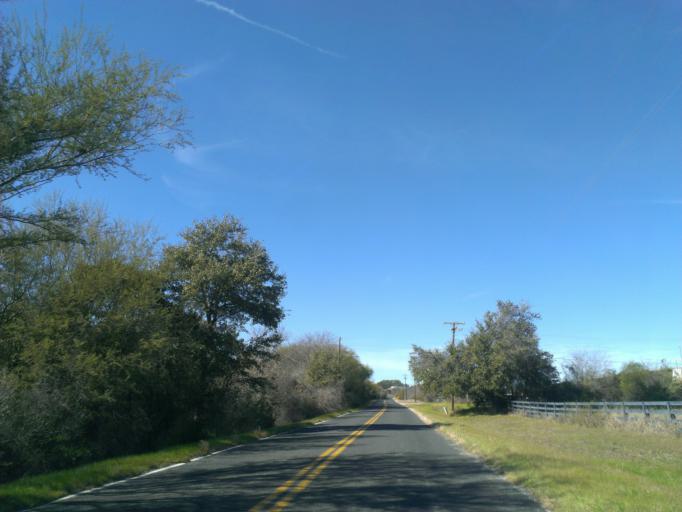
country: US
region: Texas
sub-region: Travis County
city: Briarcliff
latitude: 30.4540
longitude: -98.0917
